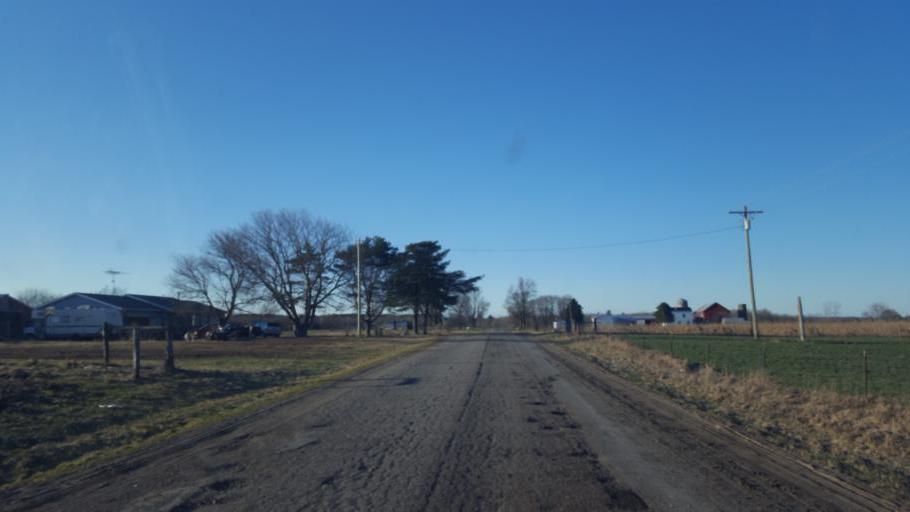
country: US
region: Michigan
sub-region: Mecosta County
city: Canadian Lakes
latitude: 43.5497
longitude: -85.3927
